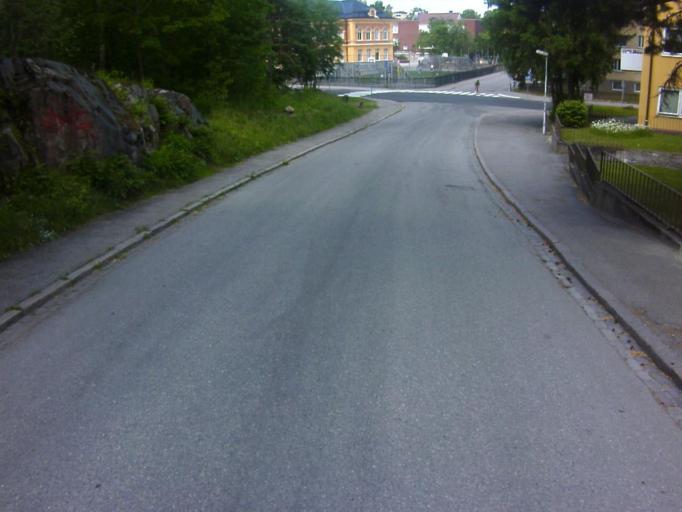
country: SE
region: Soedermanland
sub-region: Eskilstuna Kommun
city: Eskilstuna
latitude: 59.3647
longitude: 16.5020
